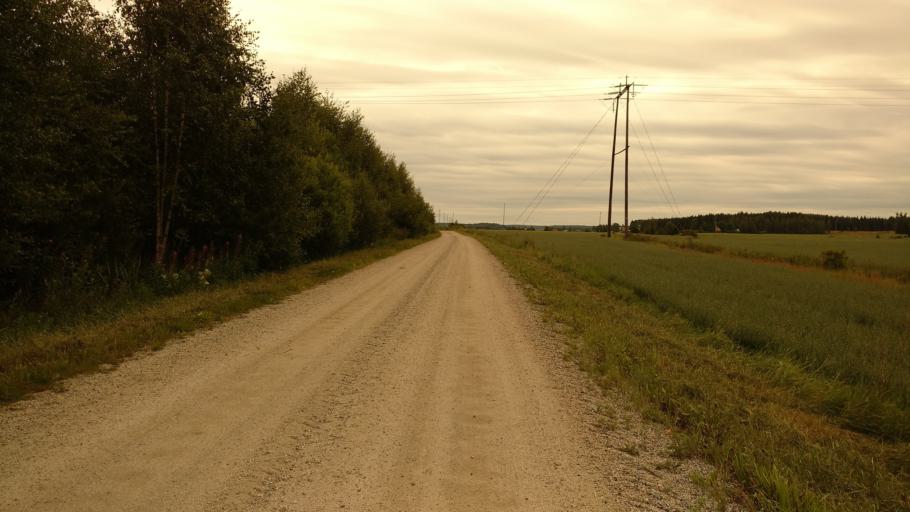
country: FI
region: Varsinais-Suomi
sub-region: Turku
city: Paimio
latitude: 60.4245
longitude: 22.8070
